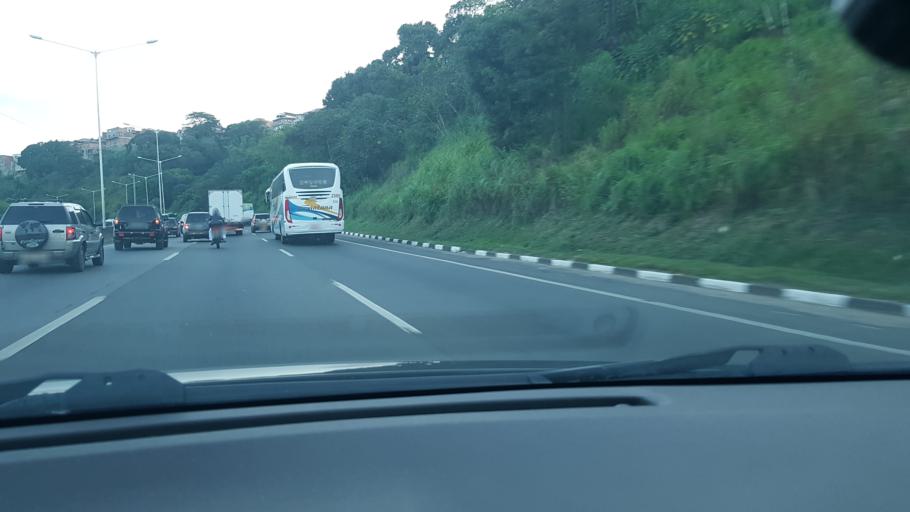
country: BR
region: Bahia
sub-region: Salvador
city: Salvador
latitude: -12.9346
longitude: -38.4721
